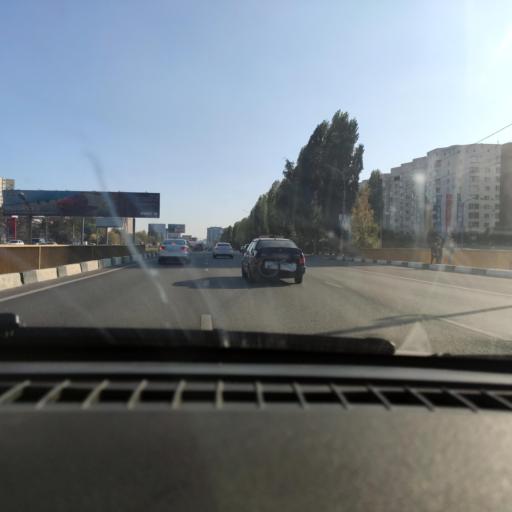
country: RU
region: Voronezj
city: Podgornoye
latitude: 51.7132
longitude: 39.1802
